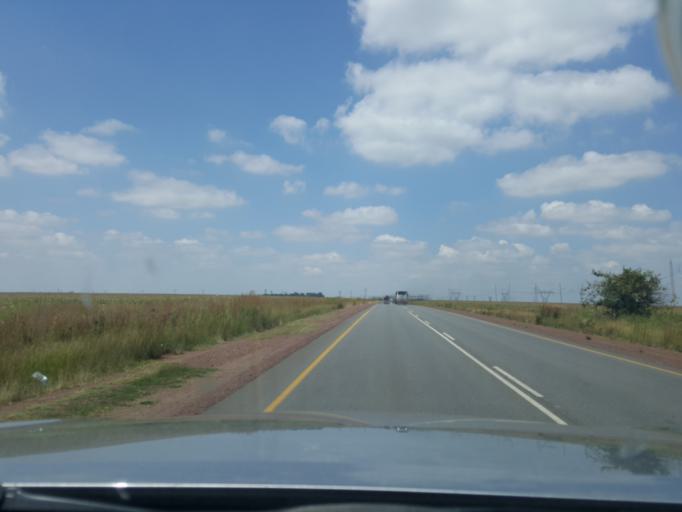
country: ZA
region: Mpumalanga
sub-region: Nkangala District Municipality
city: Witbank
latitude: -26.0146
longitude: 29.4035
